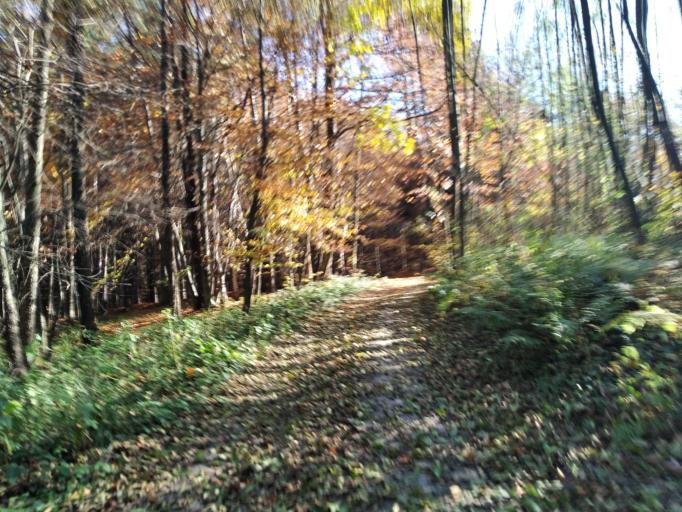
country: PL
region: Subcarpathian Voivodeship
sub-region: Powiat krosnienski
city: Leki
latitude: 49.8311
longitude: 21.6428
